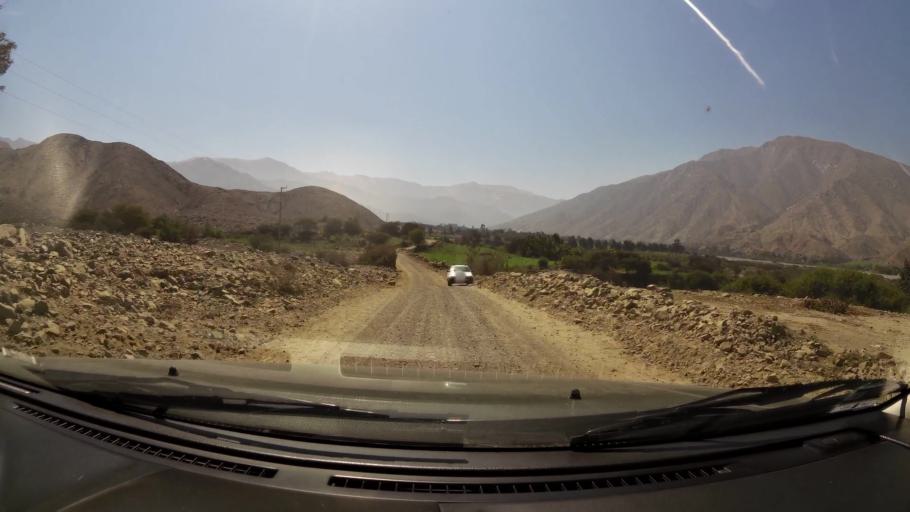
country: PE
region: Ica
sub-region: Provincia de Ica
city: Guadalupe
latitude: -13.8737
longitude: -75.6408
